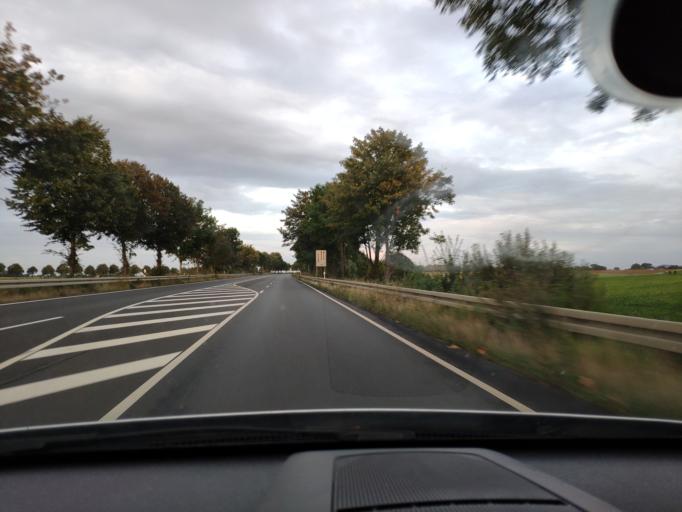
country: DE
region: North Rhine-Westphalia
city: Geilenkirchen
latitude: 50.9540
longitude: 6.1443
